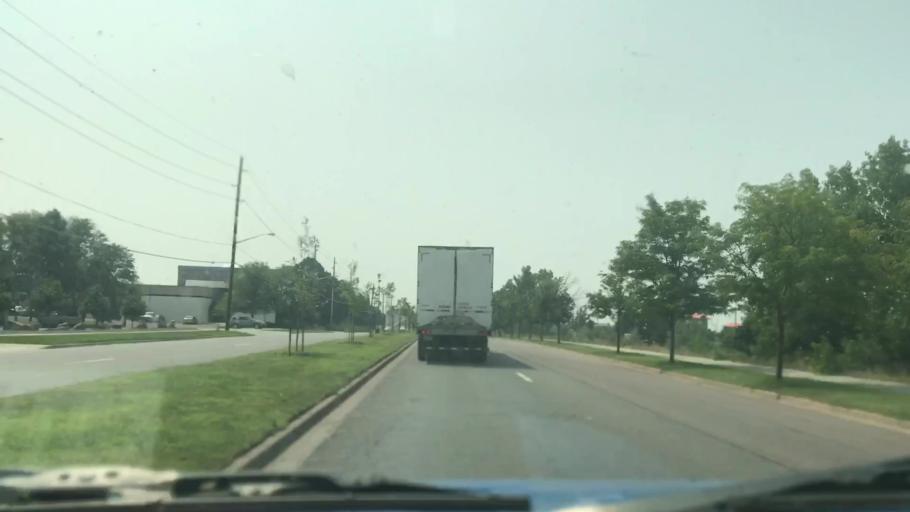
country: US
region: Colorado
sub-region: Adams County
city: Aurora
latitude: 39.7811
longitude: -104.8659
